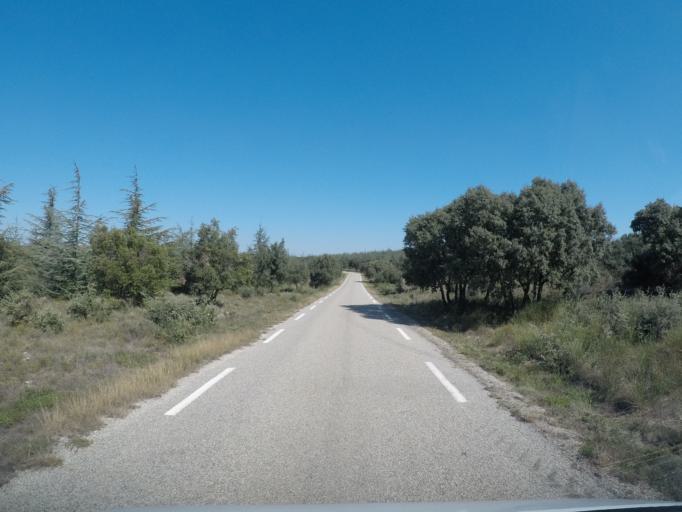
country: FR
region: Languedoc-Roussillon
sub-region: Departement du Gard
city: Saint-Victor-la-Coste
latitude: 44.0117
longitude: 4.6140
